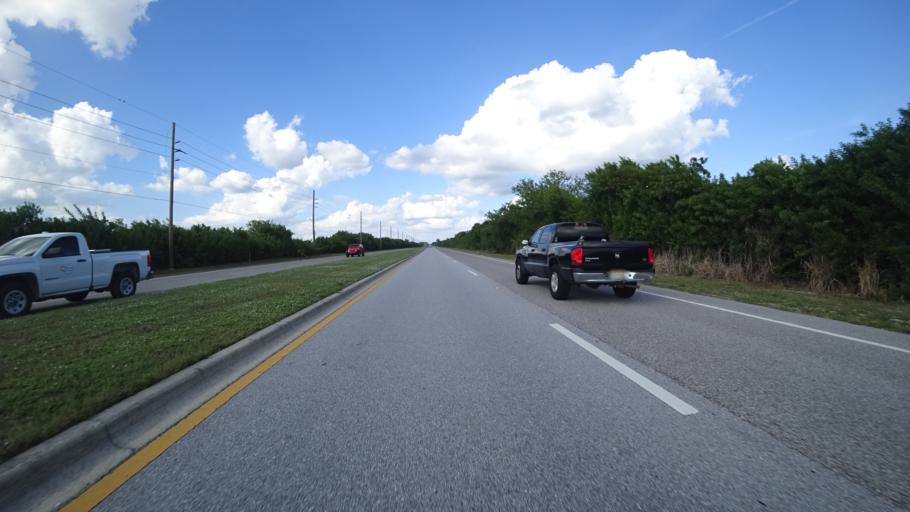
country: US
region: Florida
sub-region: Manatee County
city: Longboat Key
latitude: 27.4529
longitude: -82.6368
